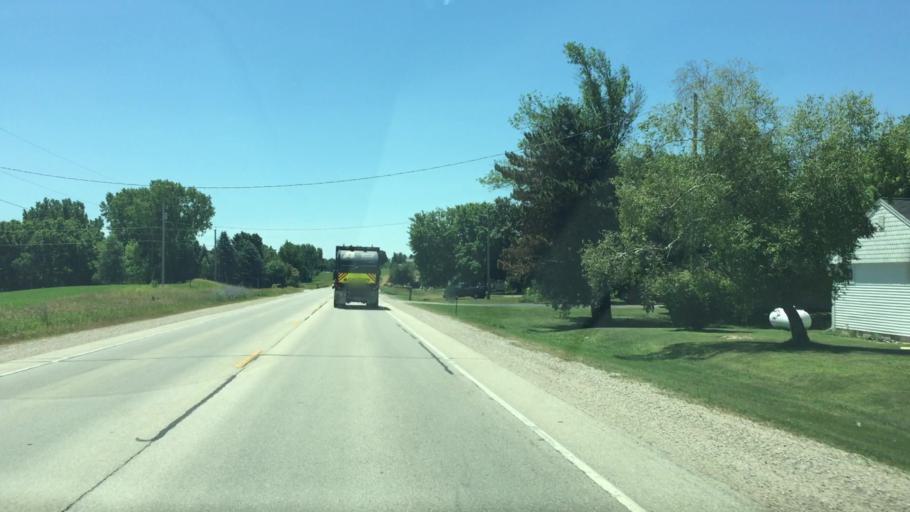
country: US
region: Wisconsin
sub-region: Calumet County
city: Chilton
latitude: 44.0529
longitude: -88.1630
